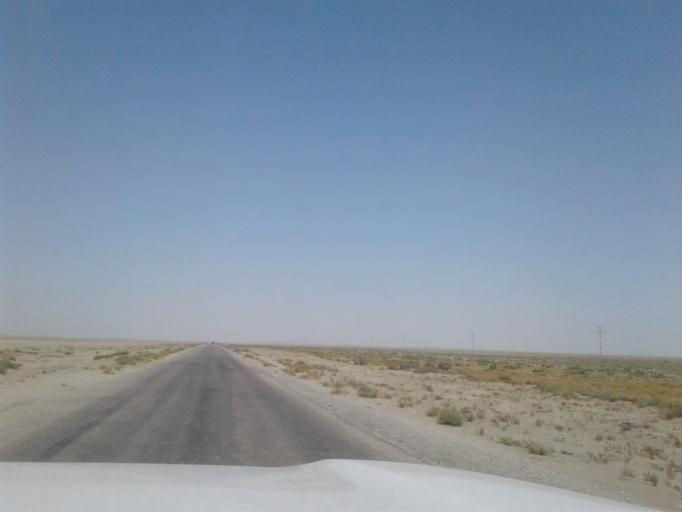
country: TM
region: Balkan
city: Gumdag
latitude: 38.3323
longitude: 54.3548
